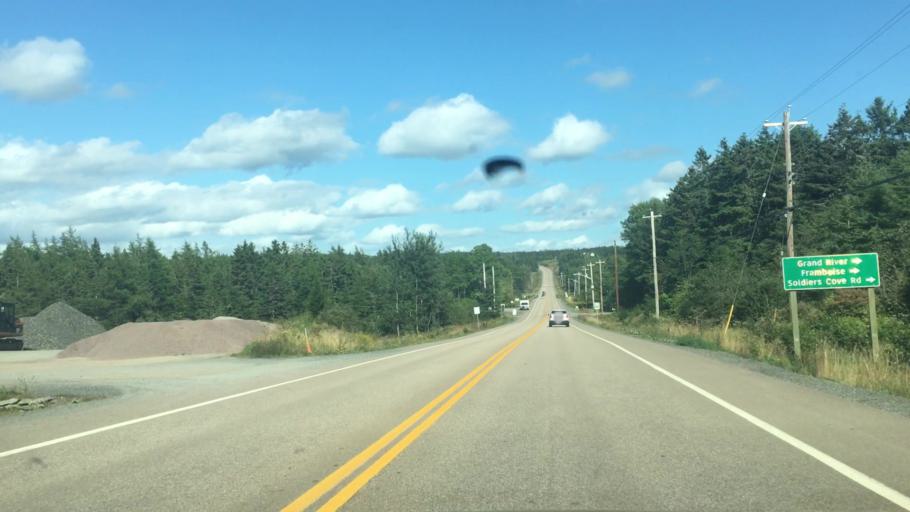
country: CA
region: Nova Scotia
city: Princeville
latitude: 45.6912
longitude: -60.7498
